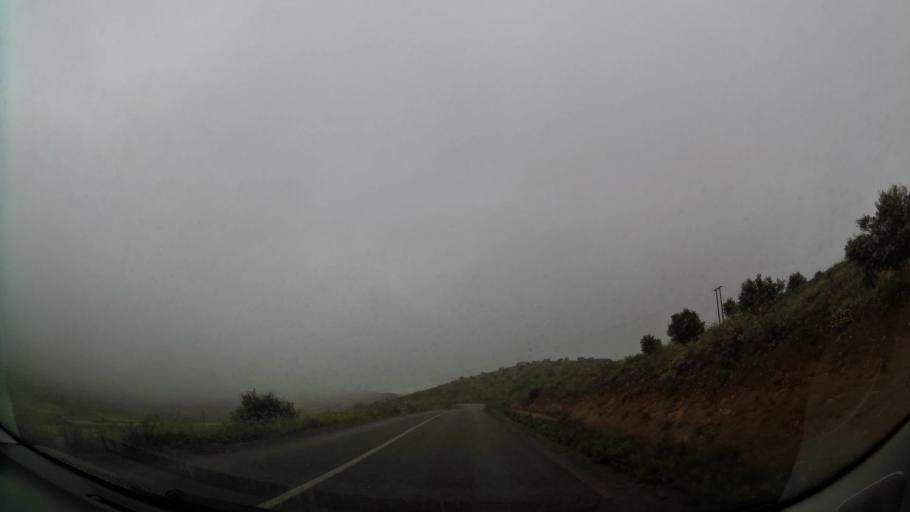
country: MA
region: Oriental
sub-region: Nador
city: Boudinar
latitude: 35.1336
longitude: -3.5970
